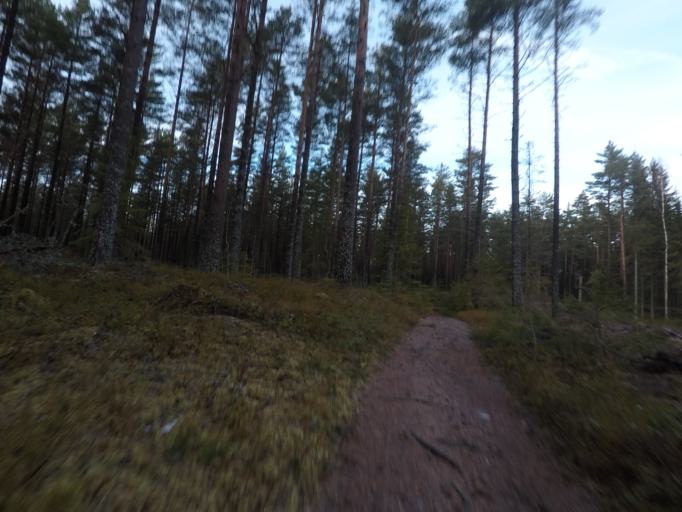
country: SE
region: Vaestmanland
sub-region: Kungsors Kommun
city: Kungsoer
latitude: 59.3456
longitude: 16.1167
